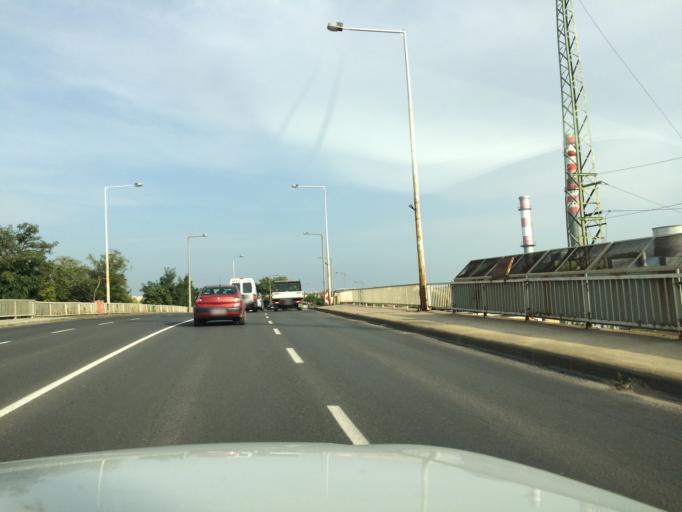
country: HU
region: Szabolcs-Szatmar-Bereg
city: Nyiregyhaza
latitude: 47.9574
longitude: 21.6962
